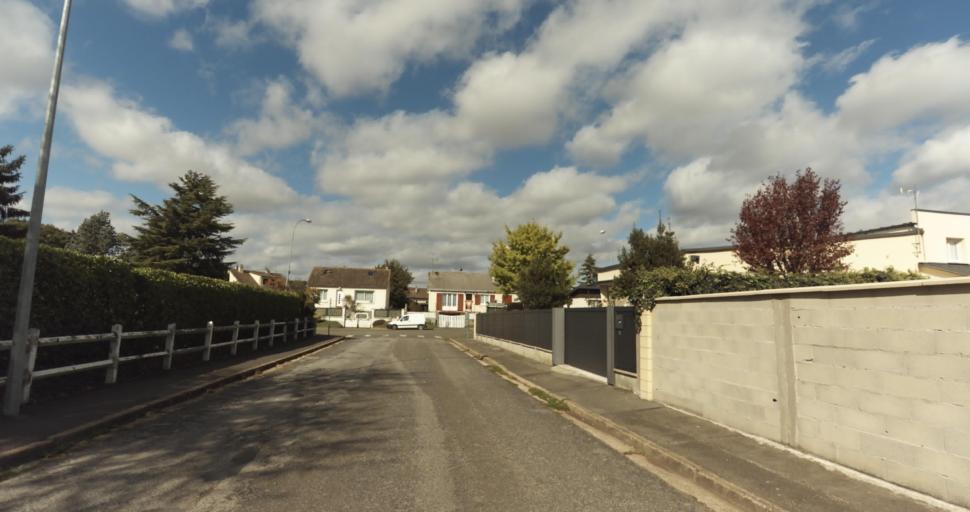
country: FR
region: Centre
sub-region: Departement d'Eure-et-Loir
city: Garnay
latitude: 48.7230
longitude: 1.3270
